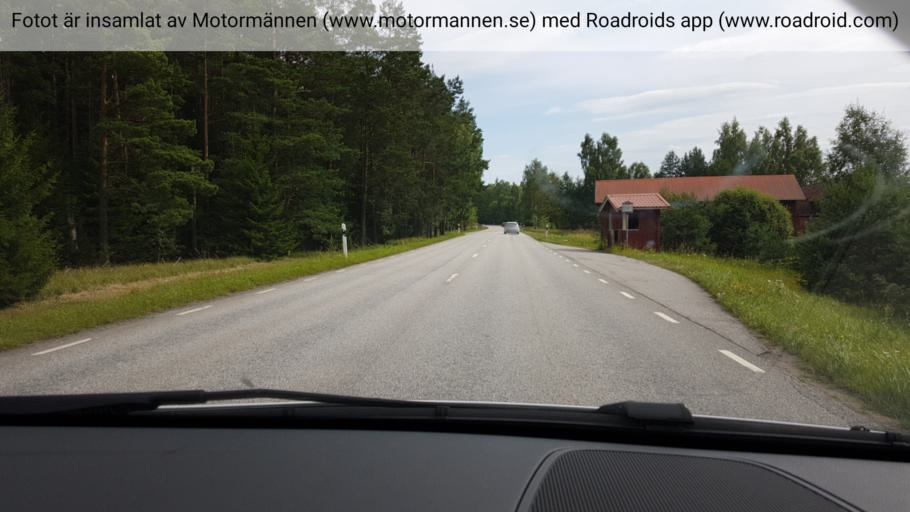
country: SE
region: Uppsala
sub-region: Osthammars Kommun
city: OEsthammar
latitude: 60.2773
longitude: 18.3023
